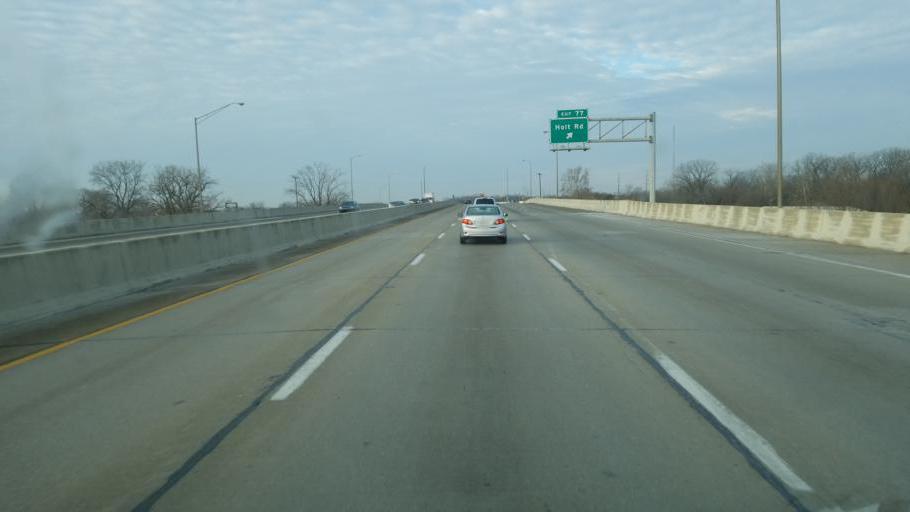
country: US
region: Indiana
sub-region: Marion County
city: Indianapolis
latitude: 39.7531
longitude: -86.2186
